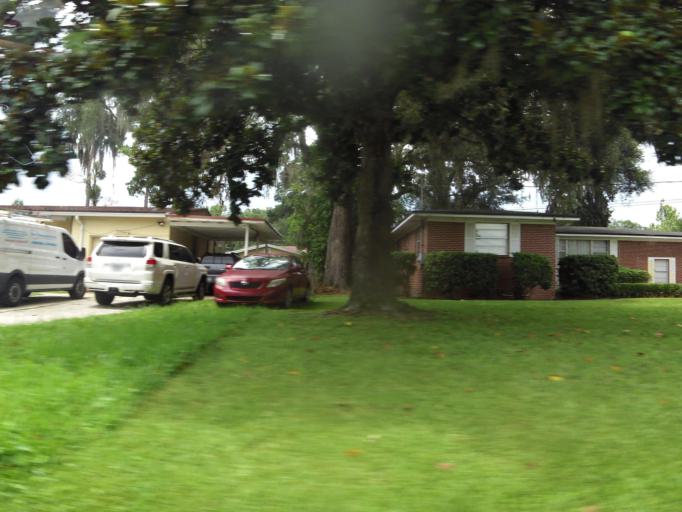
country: US
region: Florida
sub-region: Duval County
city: Jacksonville
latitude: 30.4230
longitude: -81.6822
